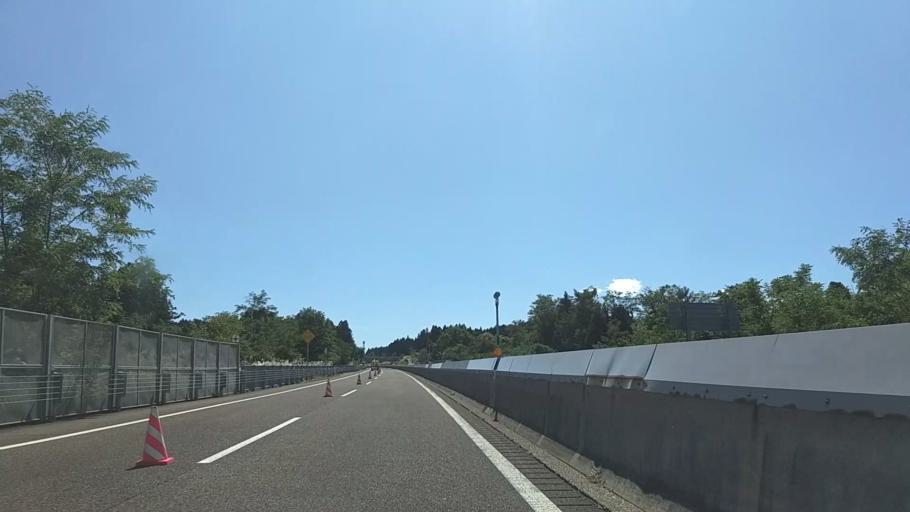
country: JP
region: Niigata
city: Arai
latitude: 36.9423
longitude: 138.2130
